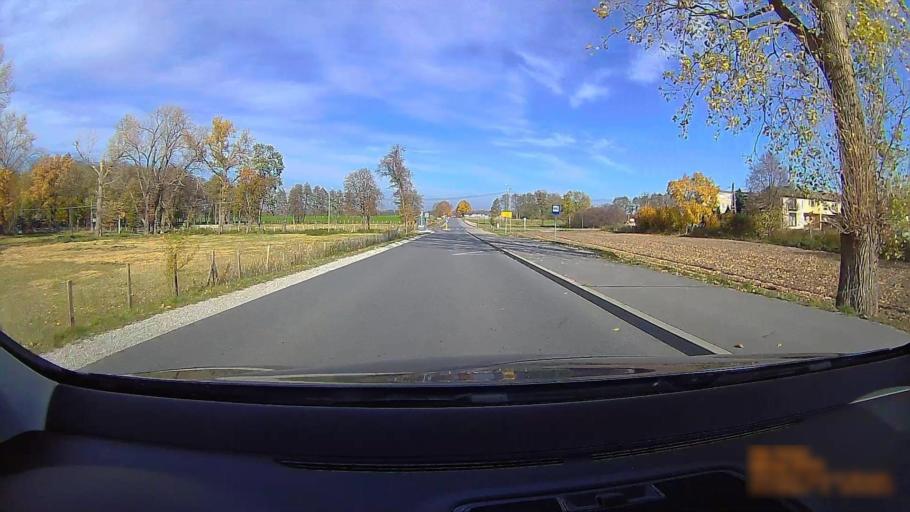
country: PL
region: Greater Poland Voivodeship
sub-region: Powiat kepinski
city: Kepno
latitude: 51.3443
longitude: 18.0238
